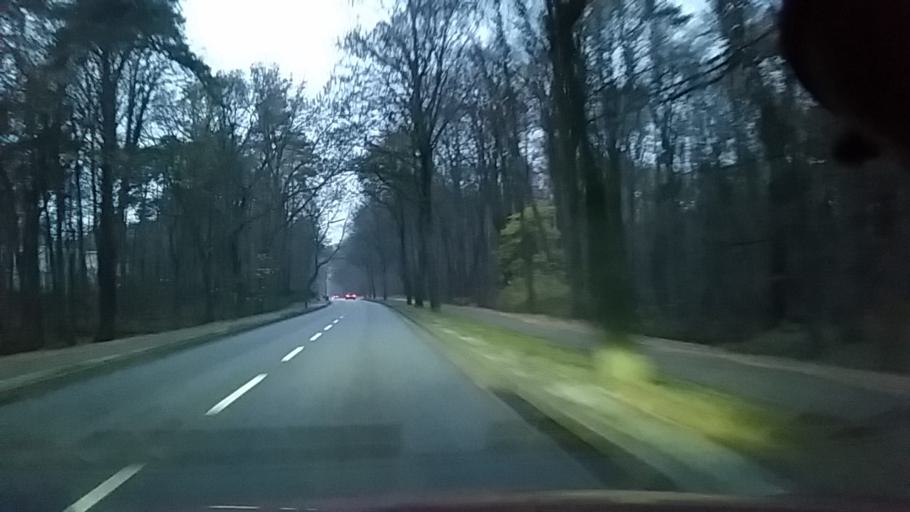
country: DE
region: Schleswig-Holstein
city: Rellingen
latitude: 53.5744
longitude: 9.7818
